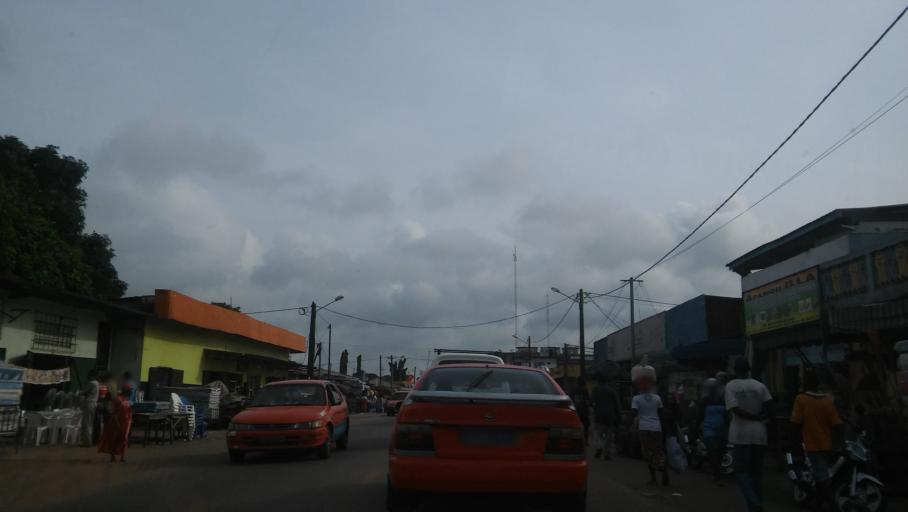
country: CI
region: Sud-Comoe
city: Grand-Bassam
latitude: 5.2086
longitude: -3.7344
